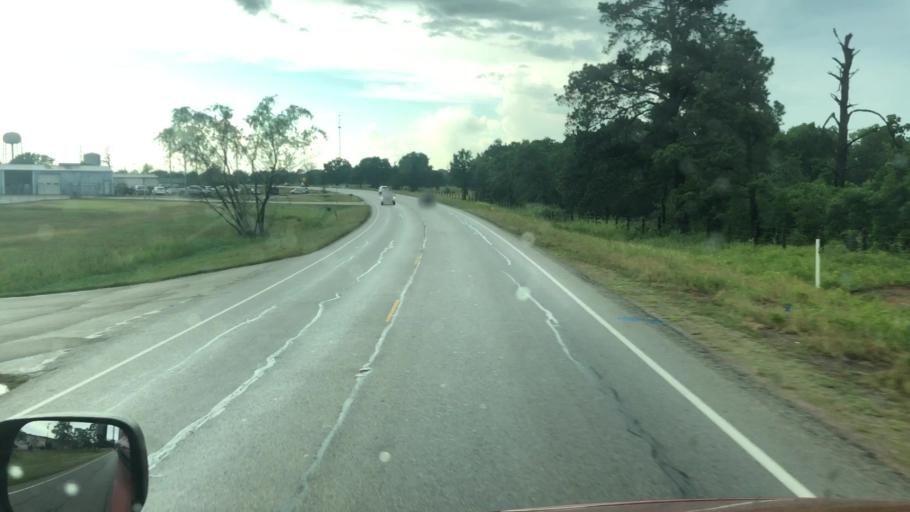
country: US
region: Texas
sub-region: Bastrop County
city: Bastrop
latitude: 30.1066
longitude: -97.2872
